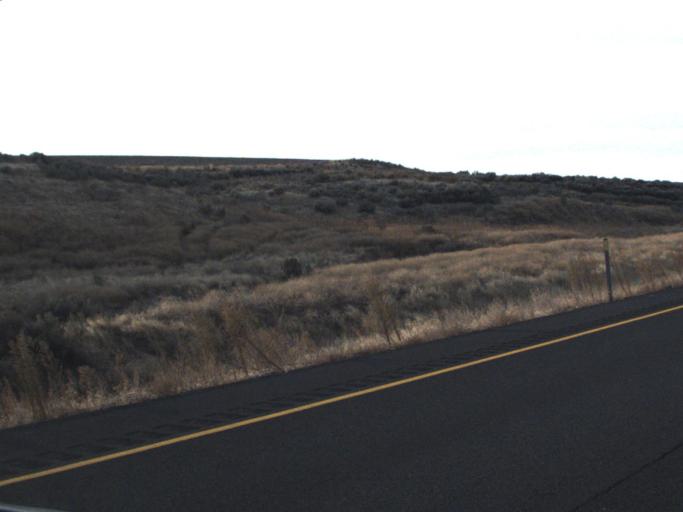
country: US
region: Washington
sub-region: Adams County
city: Ritzville
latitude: 46.9058
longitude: -118.6126
